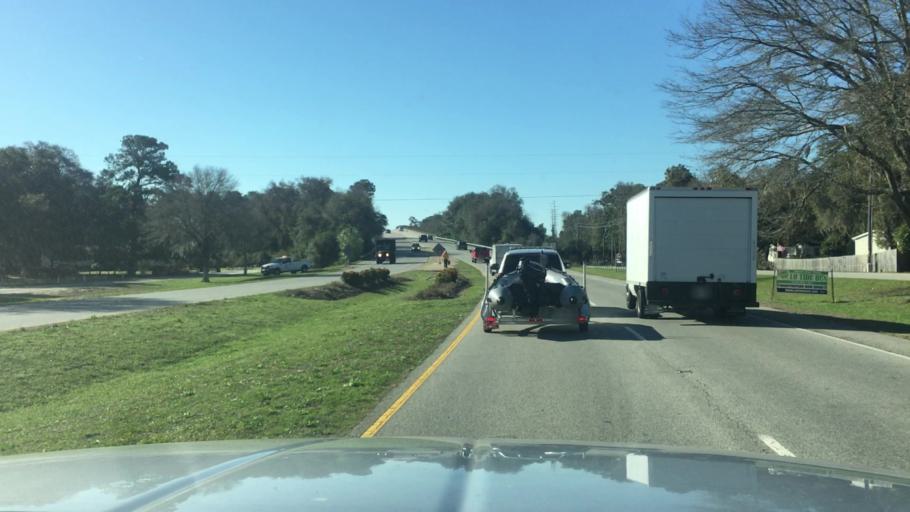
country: US
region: North Carolina
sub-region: New Hanover County
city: Sea Breeze
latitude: 34.0615
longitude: -77.8993
